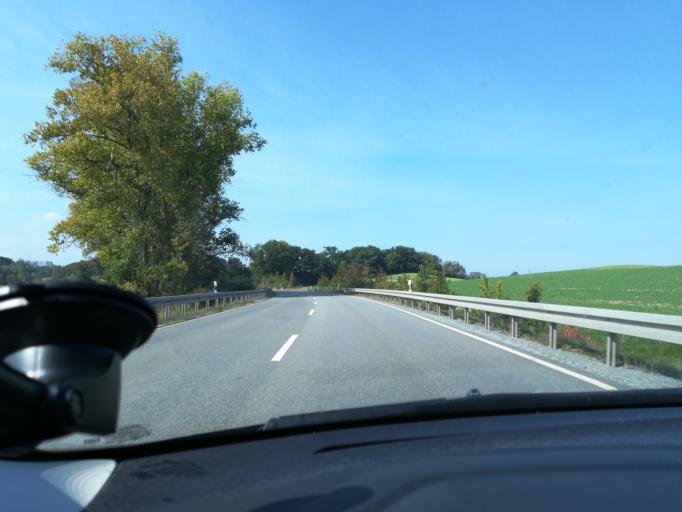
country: DE
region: Bavaria
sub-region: Upper Bavaria
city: Ebersberg
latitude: 48.0638
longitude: 11.9652
